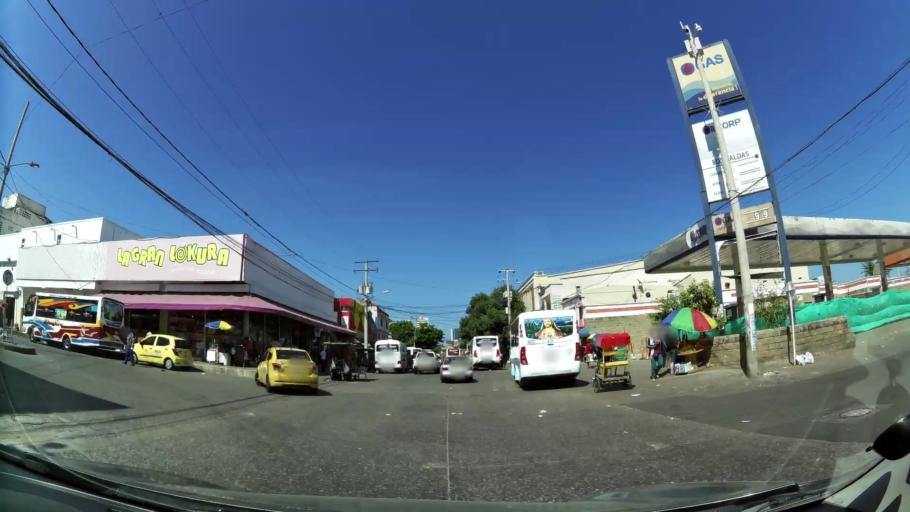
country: CO
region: Atlantico
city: Barranquilla
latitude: 10.9767
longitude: -74.7821
